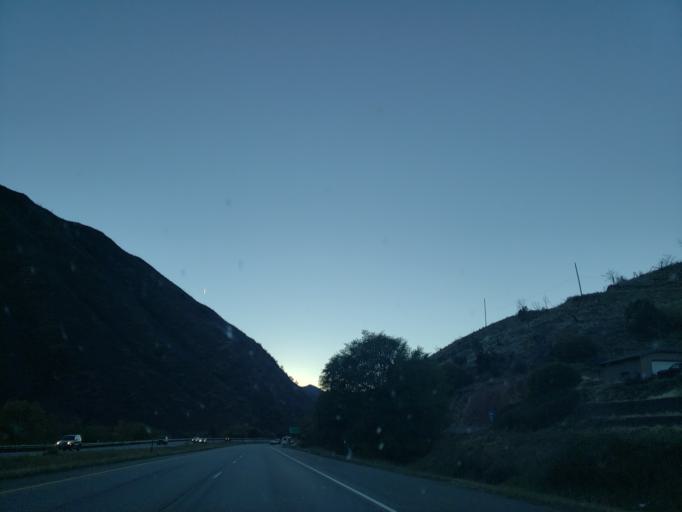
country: US
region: Colorado
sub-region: Garfield County
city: Glenwood Springs
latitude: 39.5613
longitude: -107.3728
